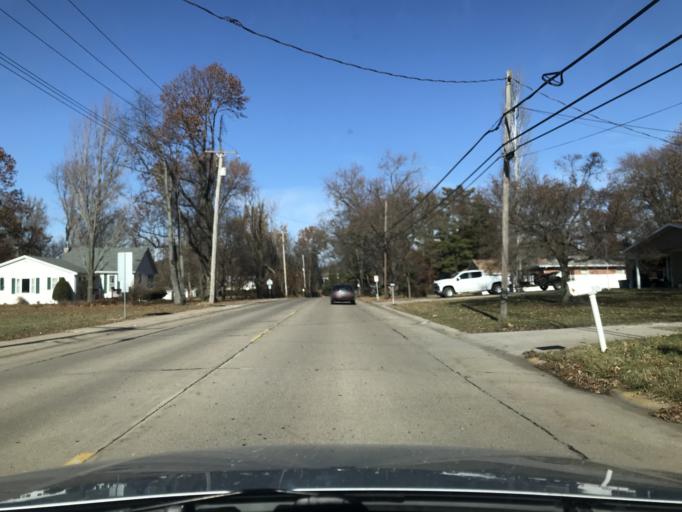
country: US
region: Illinois
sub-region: McDonough County
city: Macomb
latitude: 40.4457
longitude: -90.6708
